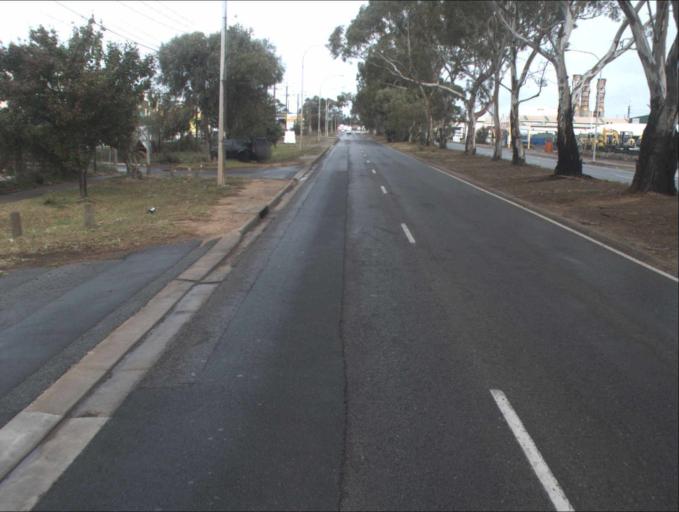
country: AU
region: South Australia
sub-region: Port Adelaide Enfield
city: Blair Athol
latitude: -34.8450
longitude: 138.5870
